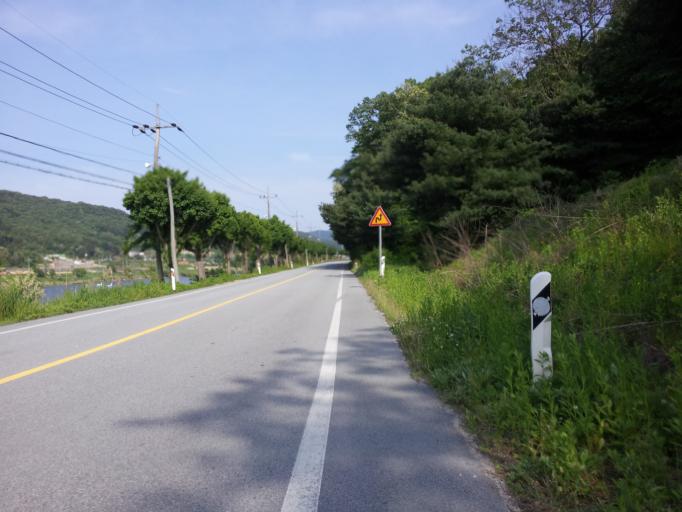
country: KR
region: Chungcheongnam-do
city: Gongju
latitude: 36.4446
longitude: 127.1848
